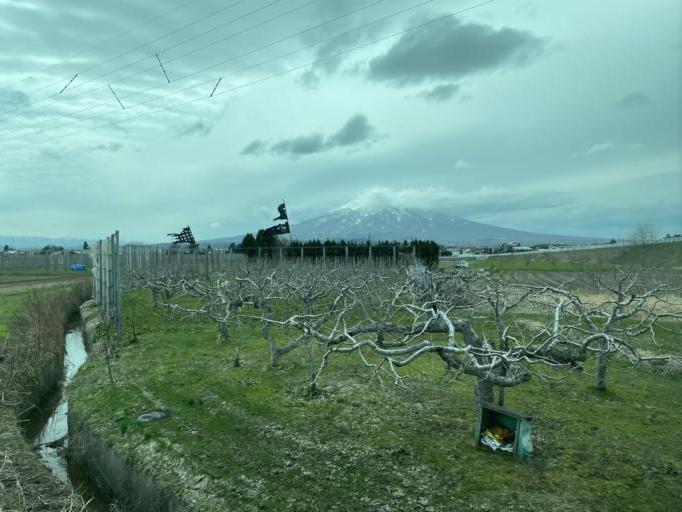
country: JP
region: Aomori
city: Goshogawara
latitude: 40.7159
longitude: 140.4470
